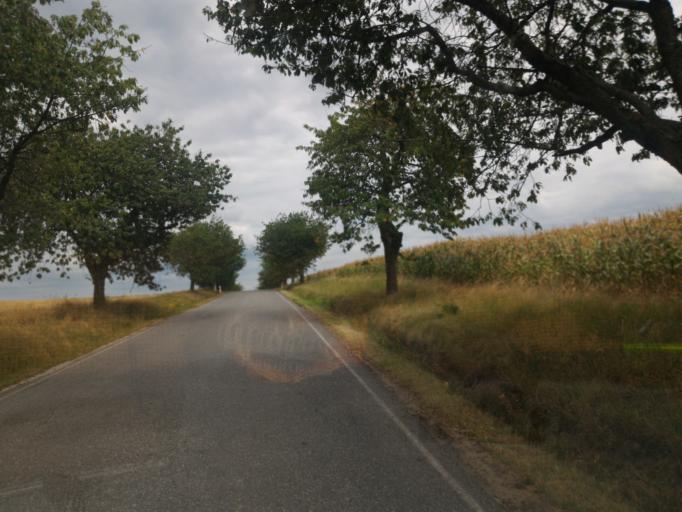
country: CZ
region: Jihocesky
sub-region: Okres Jindrichuv Hradec
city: Dacice
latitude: 49.1071
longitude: 15.4985
